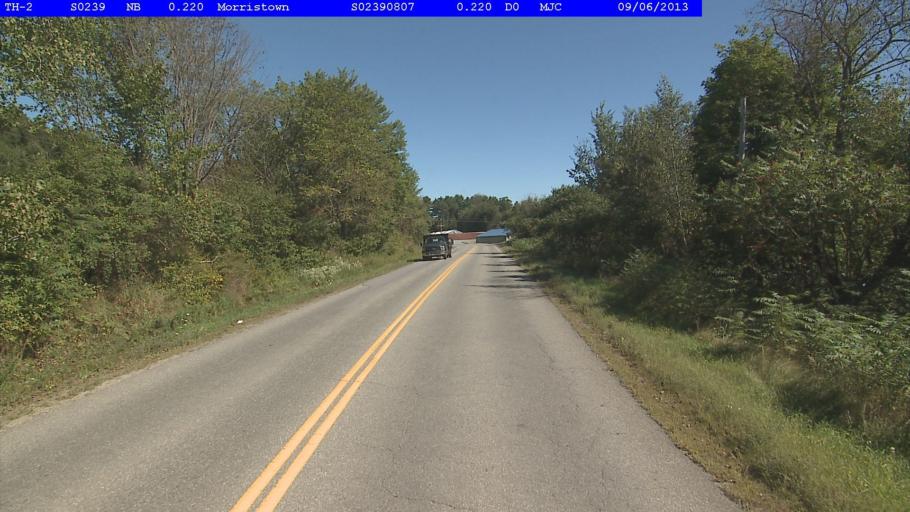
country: US
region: Vermont
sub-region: Lamoille County
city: Morristown
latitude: 44.5573
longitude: -72.6156
